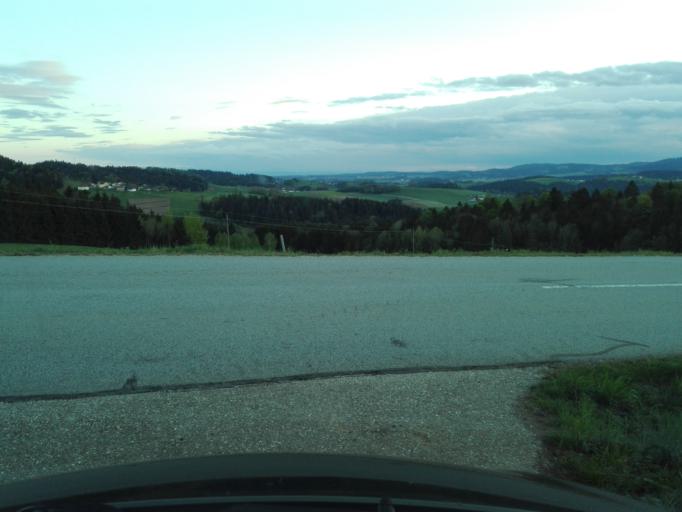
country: DE
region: Bavaria
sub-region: Lower Bavaria
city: Wegscheid
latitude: 48.5545
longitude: 13.8027
